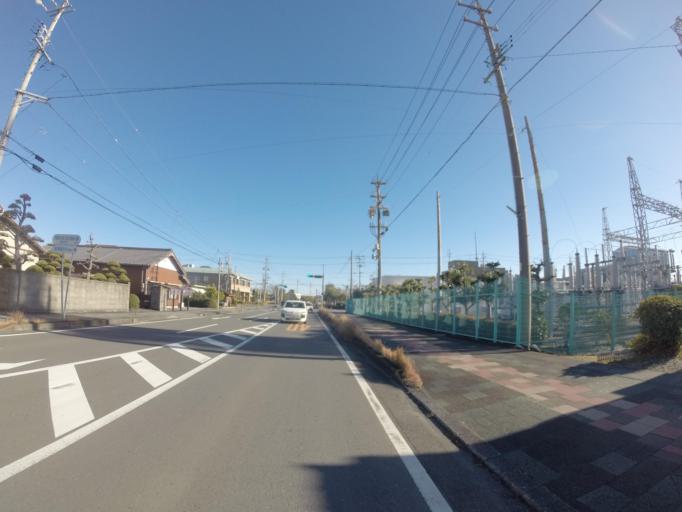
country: JP
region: Shizuoka
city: Fujieda
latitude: 34.8048
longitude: 138.2838
